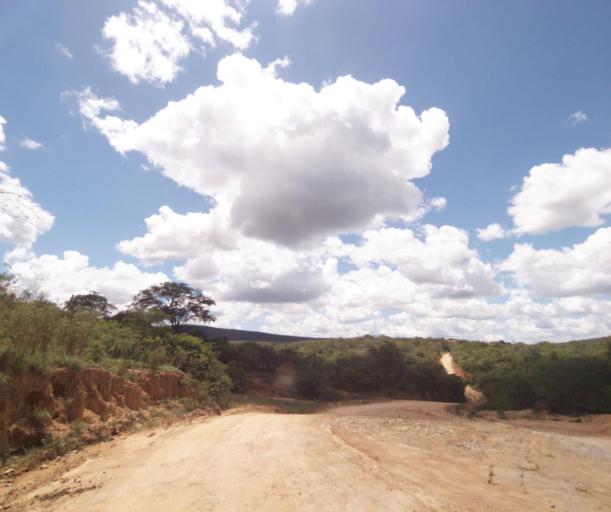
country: BR
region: Bahia
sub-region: Pocoes
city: Pocoes
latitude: -14.3895
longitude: -40.5483
